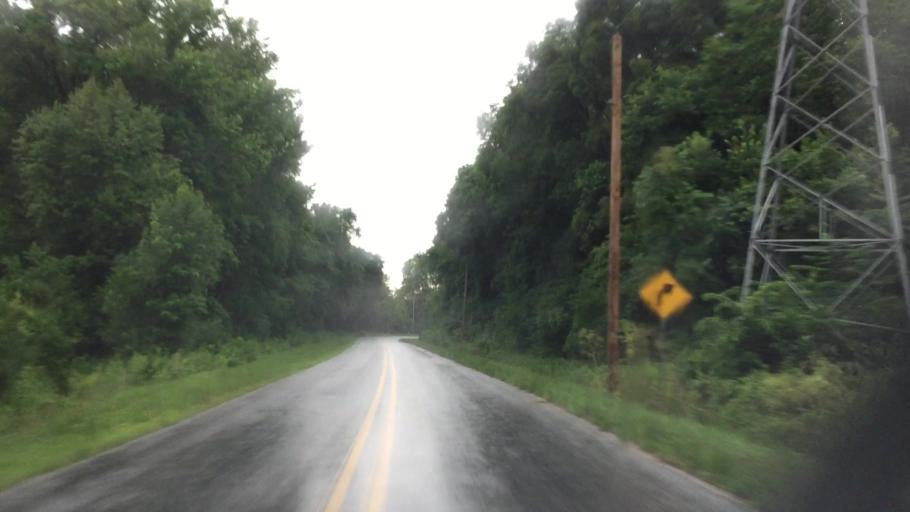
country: US
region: Iowa
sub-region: Lee County
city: Fort Madison
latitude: 40.6097
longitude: -91.2806
